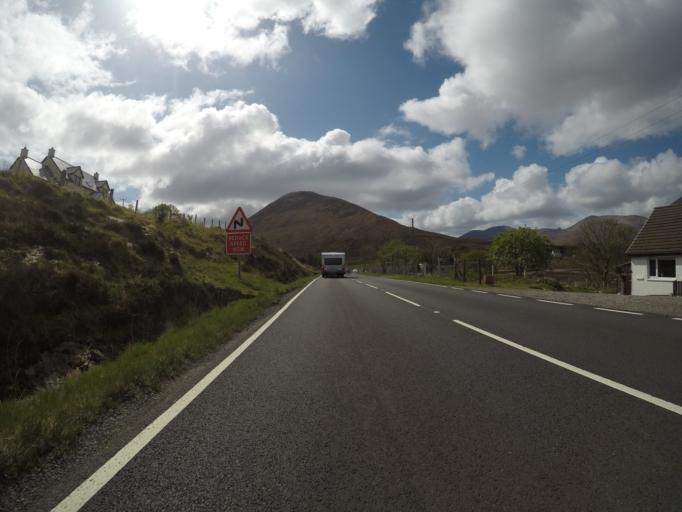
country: GB
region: Scotland
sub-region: Highland
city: Portree
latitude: 57.2777
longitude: -6.0412
